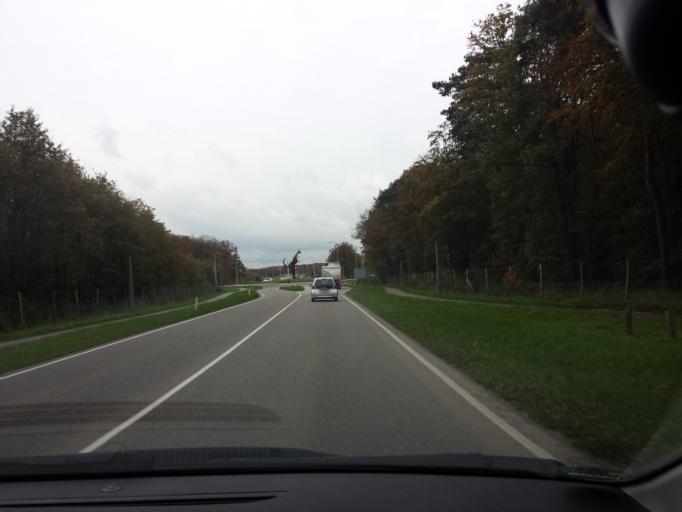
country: NL
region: Limburg
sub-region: Gemeente Beesel
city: Reuver
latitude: 51.2681
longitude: 6.0697
